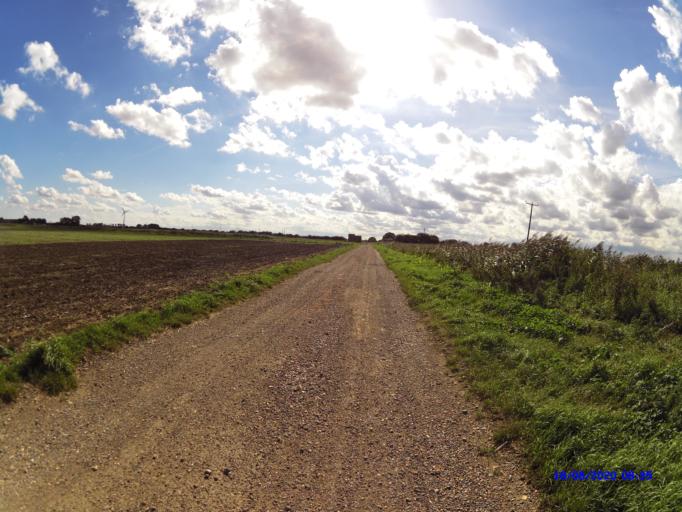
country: GB
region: England
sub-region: Cambridgeshire
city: Ramsey
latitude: 52.4961
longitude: -0.0902
